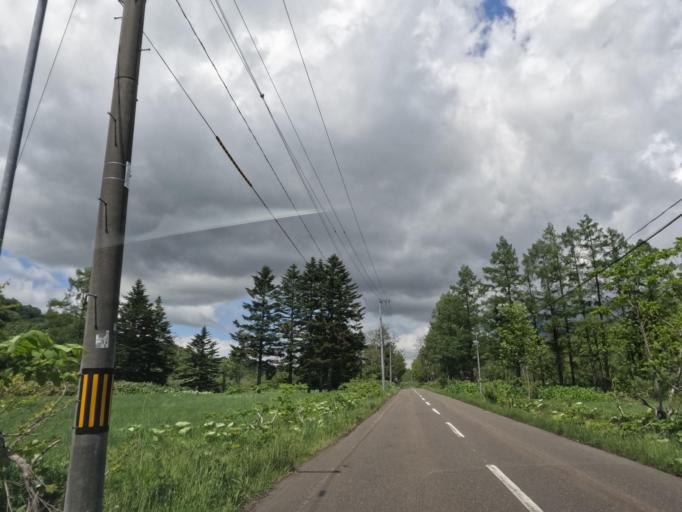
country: JP
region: Hokkaido
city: Tobetsu
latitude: 43.4400
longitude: 141.5825
